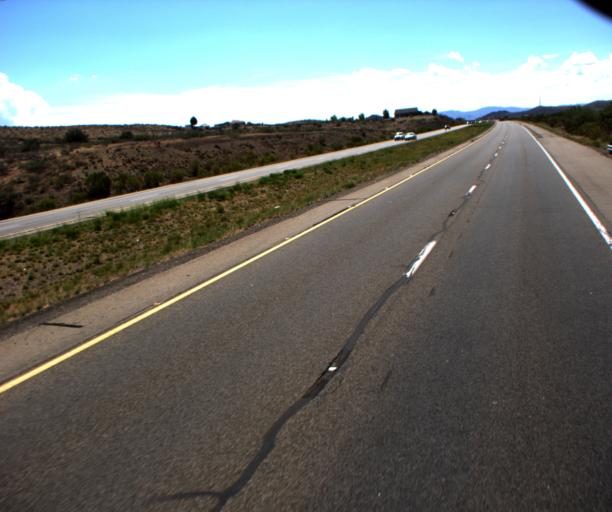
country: US
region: Arizona
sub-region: Yavapai County
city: Spring Valley
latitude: 34.3619
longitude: -112.1739
